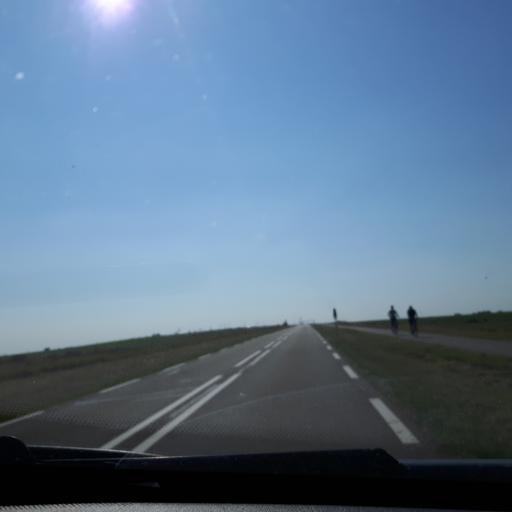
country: NL
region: Zeeland
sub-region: Gemeente Reimerswaal
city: Yerseke
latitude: 51.5007
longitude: 4.0152
